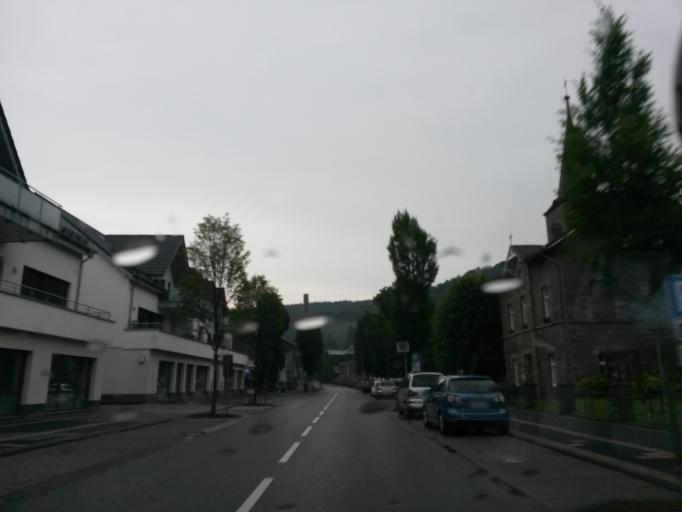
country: DE
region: North Rhine-Westphalia
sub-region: Regierungsbezirk Koln
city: Engelskirchen
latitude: 50.9854
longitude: 7.4094
